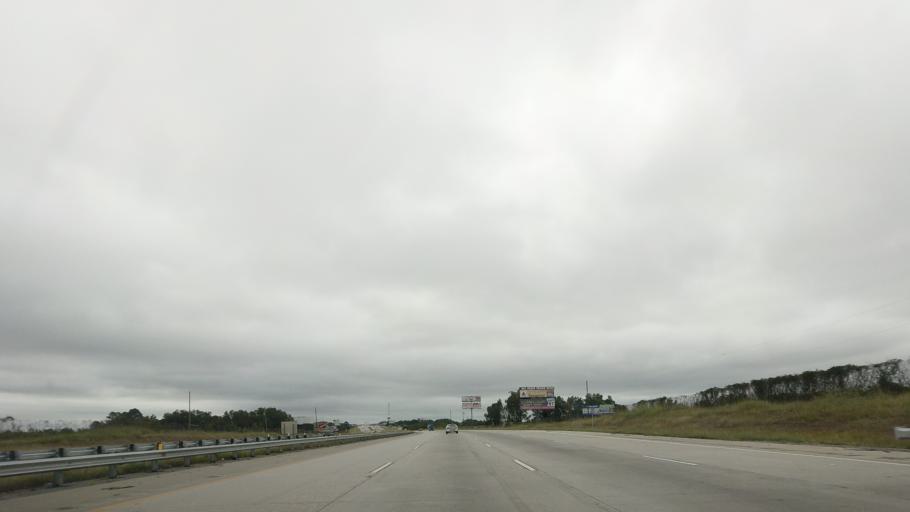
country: US
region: Georgia
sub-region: Dooly County
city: Unadilla
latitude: 32.2571
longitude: -83.7486
